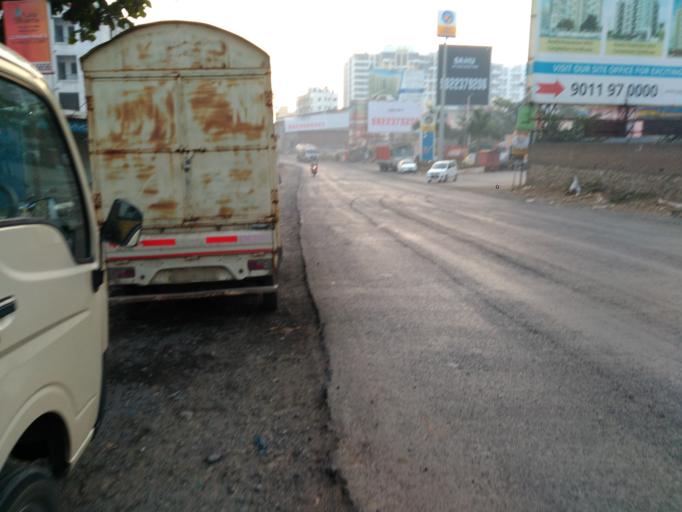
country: IN
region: Maharashtra
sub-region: Pune Division
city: Pune
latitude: 18.4494
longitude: 73.9039
